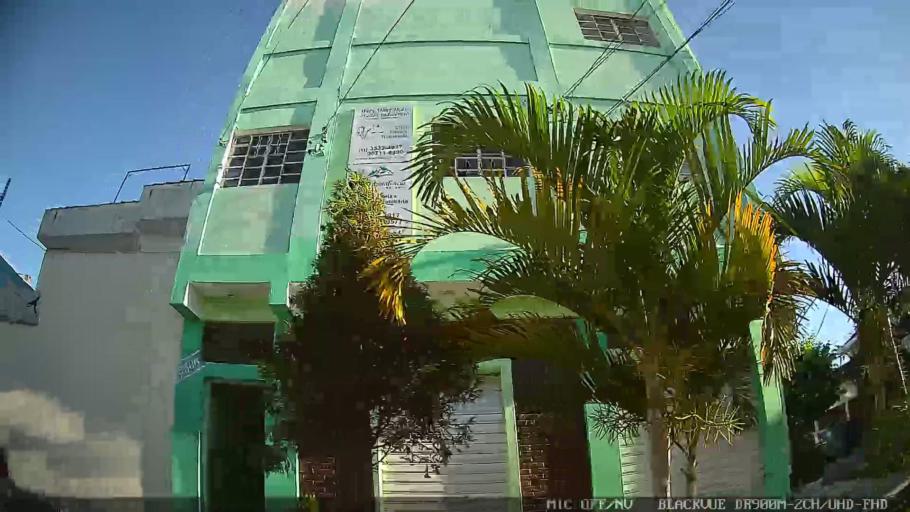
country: BR
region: Sao Paulo
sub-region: Guarulhos
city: Guarulhos
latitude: -23.5332
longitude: -46.5158
